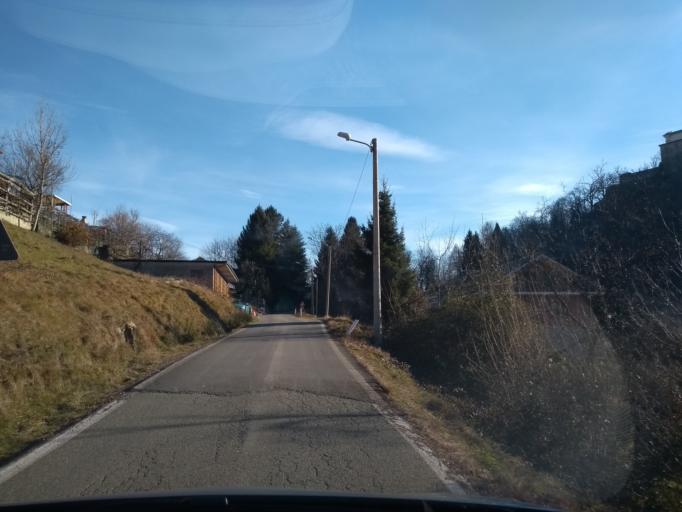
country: IT
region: Piedmont
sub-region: Provincia di Torino
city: Traves
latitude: 45.2804
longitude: 7.4407
